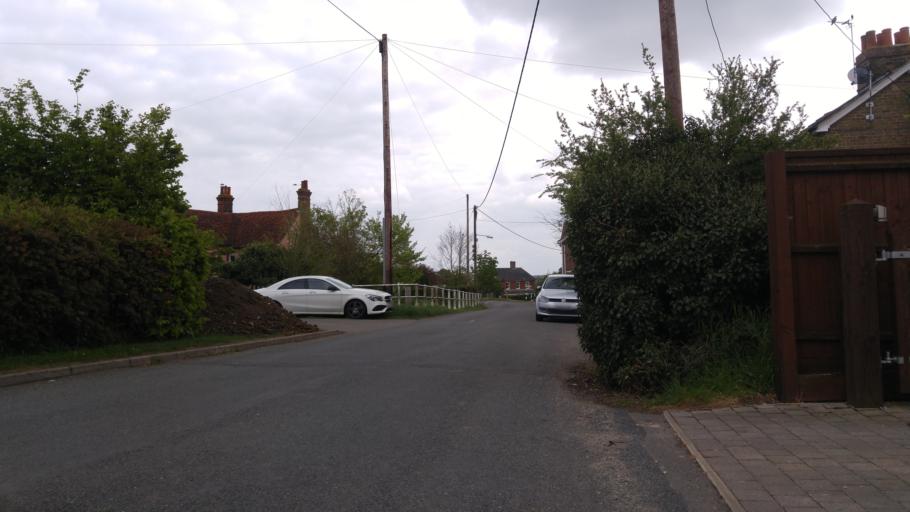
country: GB
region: England
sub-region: Essex
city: Earls Colne
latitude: 51.9434
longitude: 0.6909
